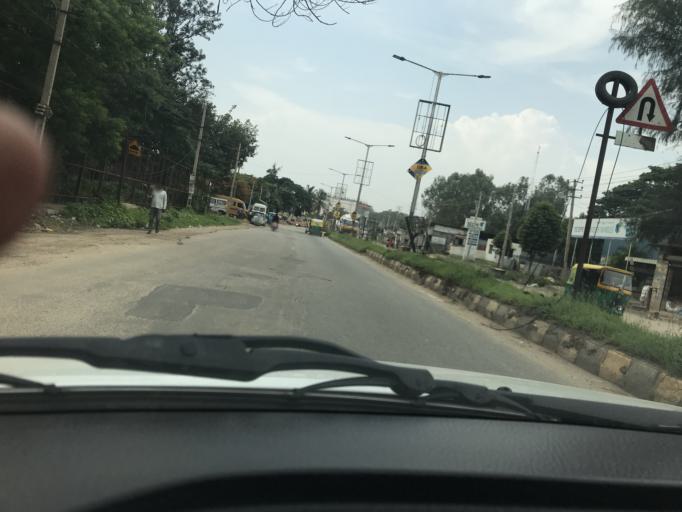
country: IN
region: Karnataka
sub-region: Bangalore Urban
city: Yelahanka
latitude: 13.0738
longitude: 77.6514
